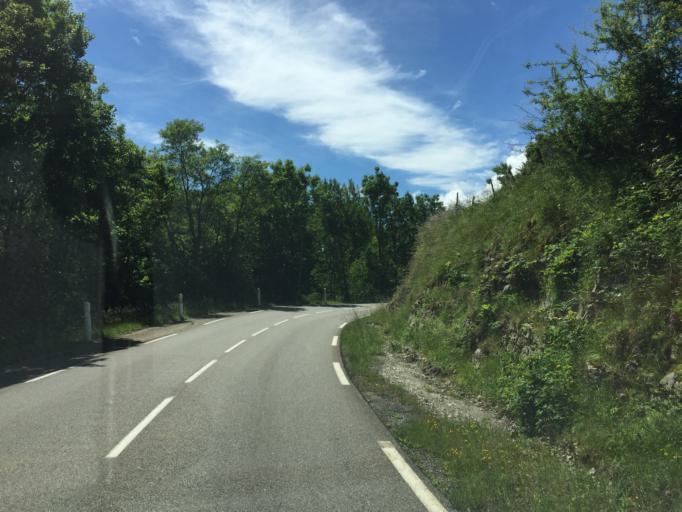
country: FR
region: Rhone-Alpes
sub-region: Departement de la Savoie
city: Saint-Baldoph
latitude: 45.5075
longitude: 5.9238
